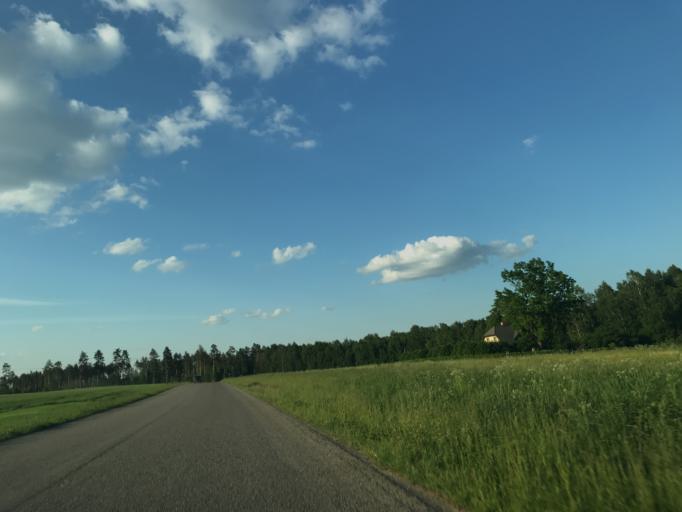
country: LV
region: Lecava
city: Iecava
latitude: 56.6296
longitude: 24.2677
